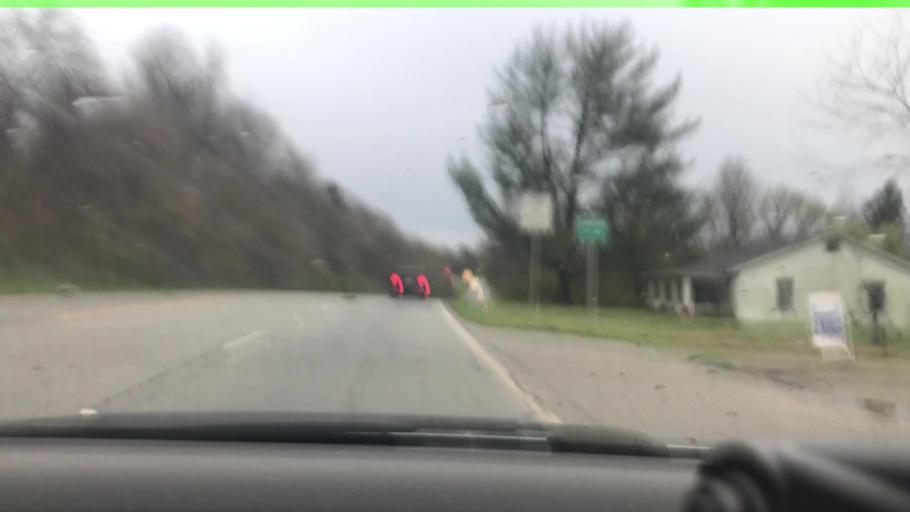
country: US
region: Georgia
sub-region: Oglethorpe County
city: Lexington
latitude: 33.8844
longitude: -83.1657
